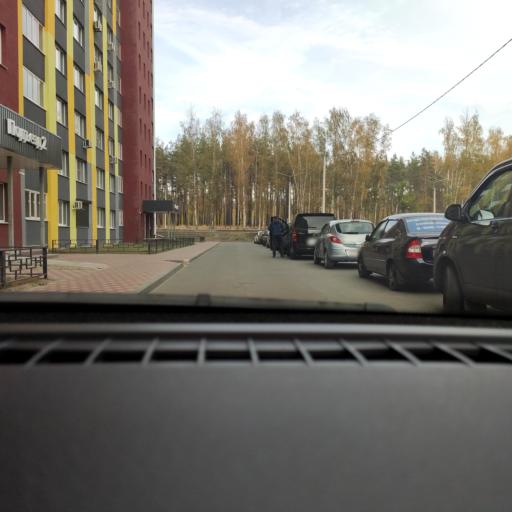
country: RU
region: Voronezj
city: Somovo
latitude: 51.7414
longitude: 39.3174
